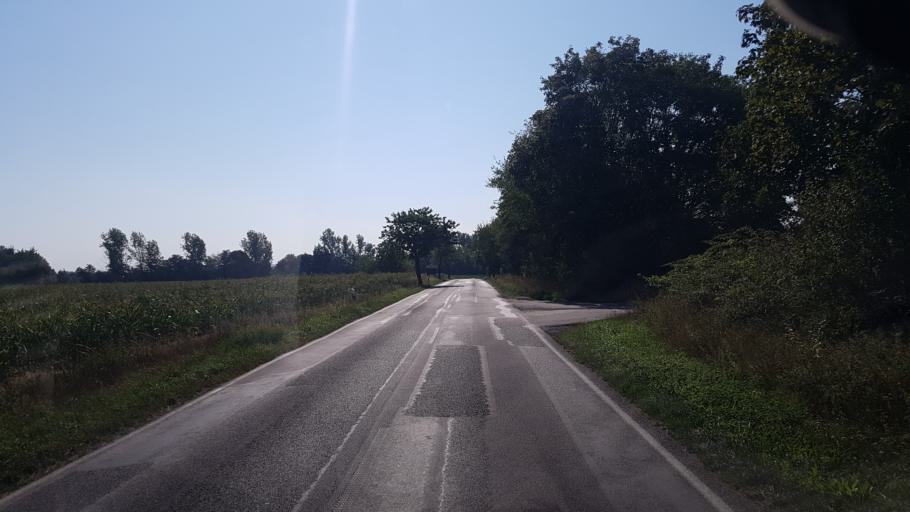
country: DE
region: Brandenburg
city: Hirschfeld
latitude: 51.3935
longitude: 13.6061
